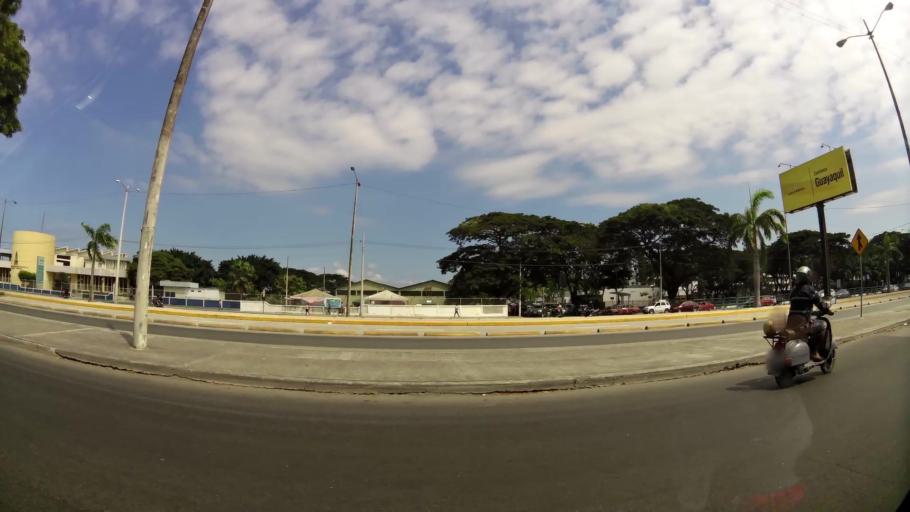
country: EC
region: Guayas
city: Guayaquil
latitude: -2.2344
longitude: -79.8967
